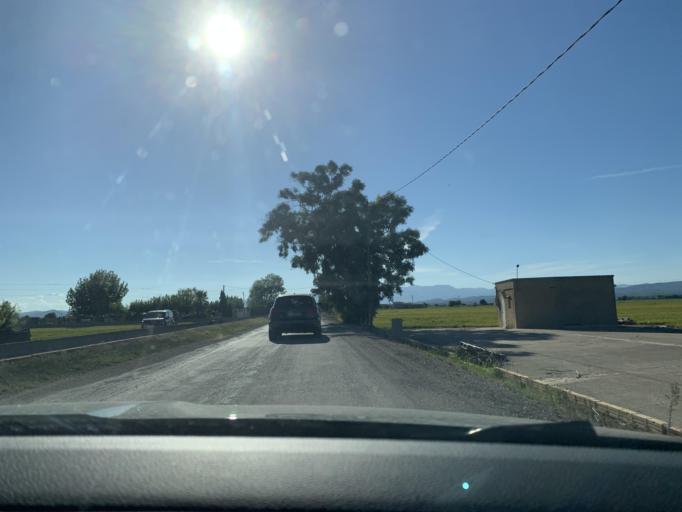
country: ES
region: Catalonia
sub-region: Provincia de Tarragona
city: Deltebre
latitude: 40.7481
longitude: 0.7323
